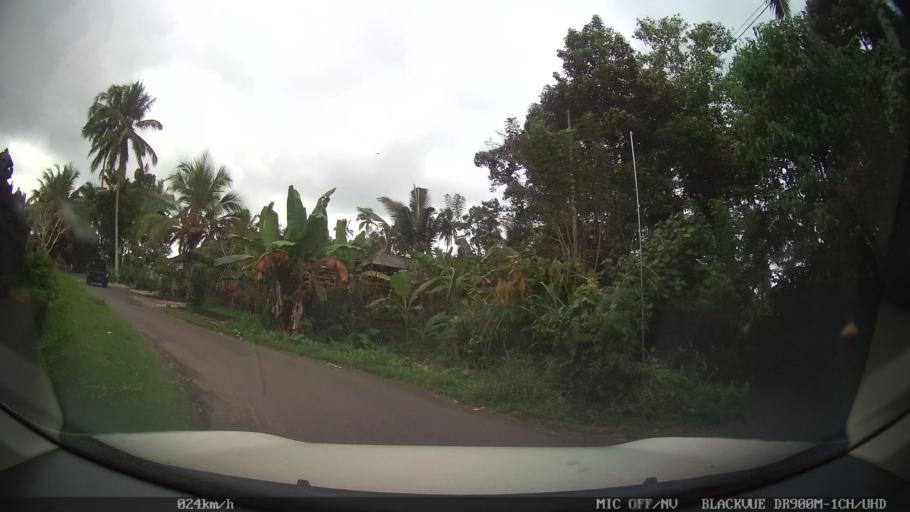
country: ID
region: Bali
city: Banjar Wangsian
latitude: -8.4439
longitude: 115.4253
